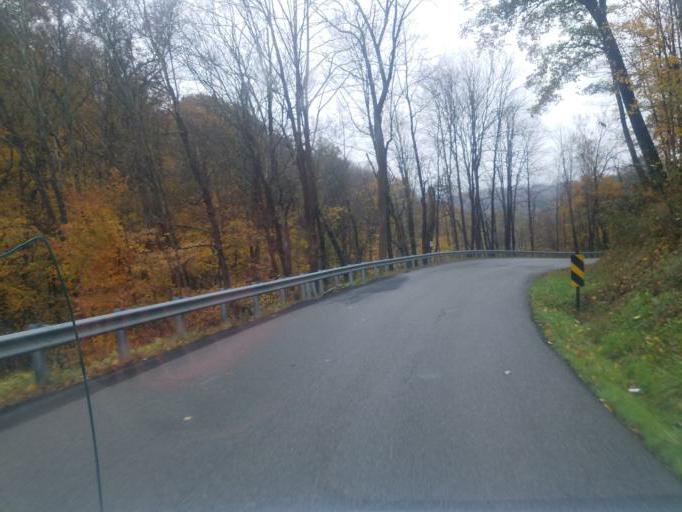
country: US
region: Ohio
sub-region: Morgan County
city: McConnelsville
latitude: 39.6448
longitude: -81.8627
